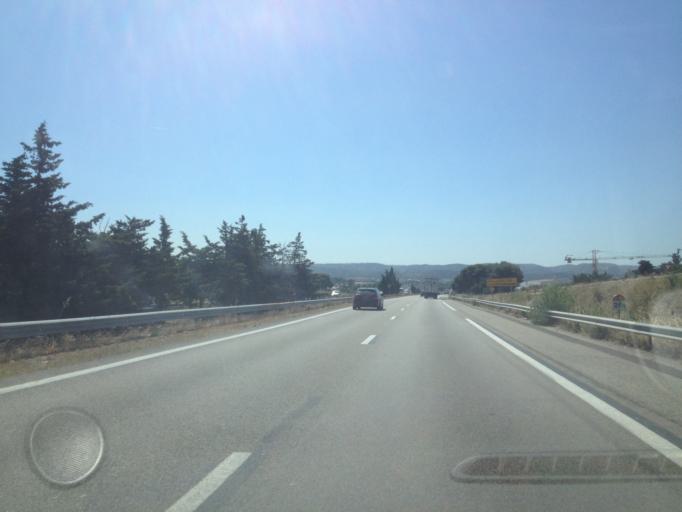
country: FR
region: Provence-Alpes-Cote d'Azur
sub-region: Departement des Bouches-du-Rhone
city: Vitrolles
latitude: 43.4394
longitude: 5.2500
